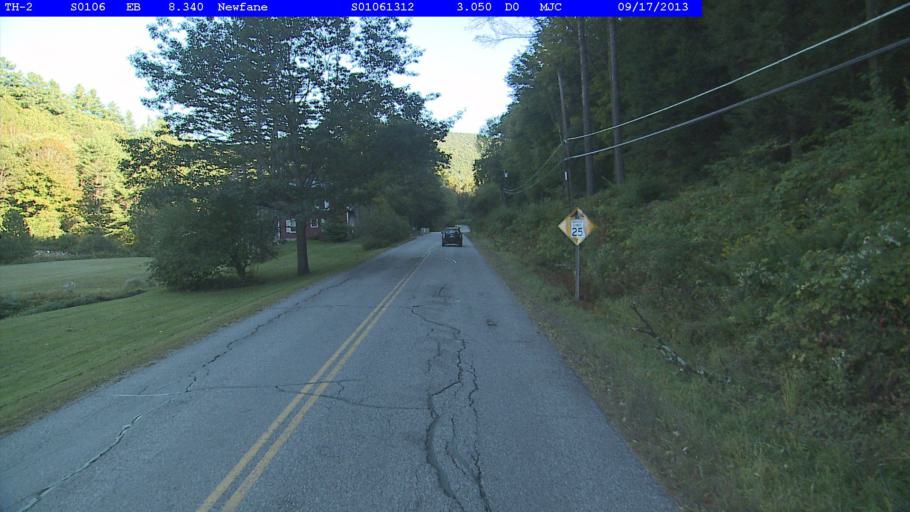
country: US
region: Vermont
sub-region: Windham County
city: Newfane
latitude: 42.9362
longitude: -72.7159
